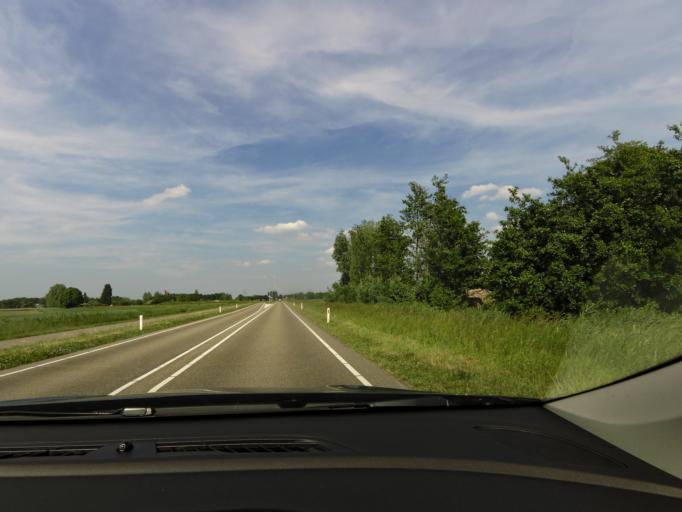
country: NL
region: South Holland
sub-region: Gemeente Spijkenisse
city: Spijkenisse
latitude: 51.8013
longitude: 4.3413
